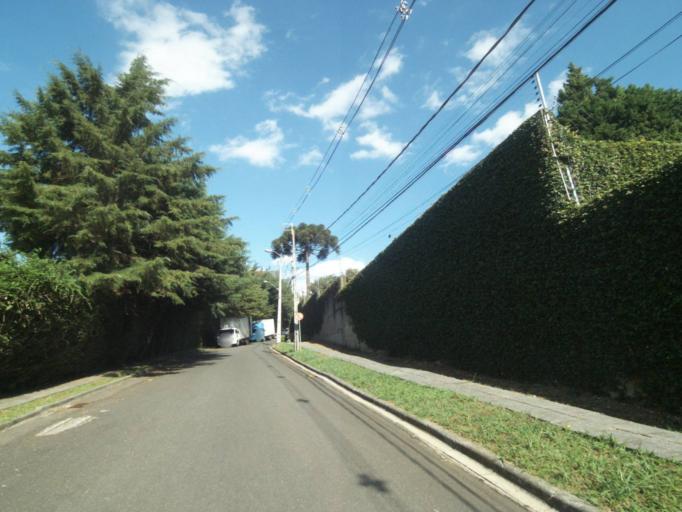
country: BR
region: Parana
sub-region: Curitiba
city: Curitiba
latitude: -25.4408
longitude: -49.3241
